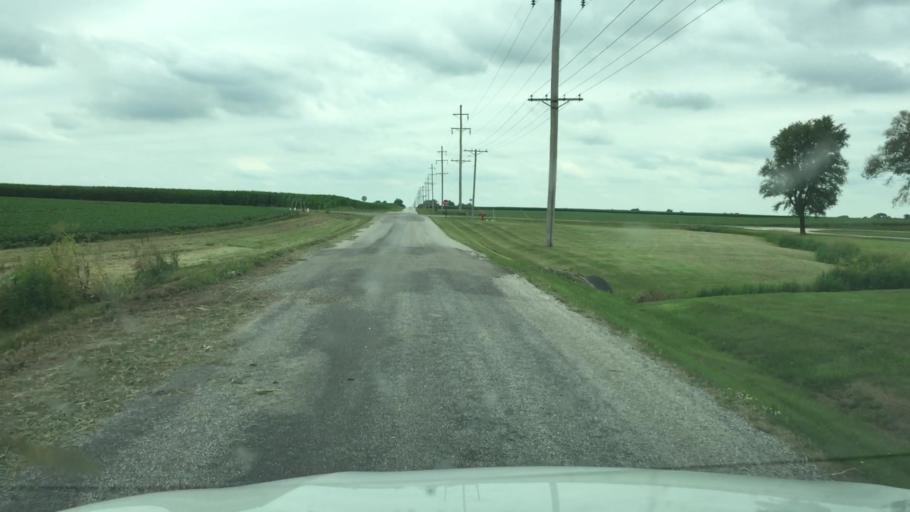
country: US
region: Illinois
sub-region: Hancock County
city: Carthage
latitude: 40.3428
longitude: -91.0823
